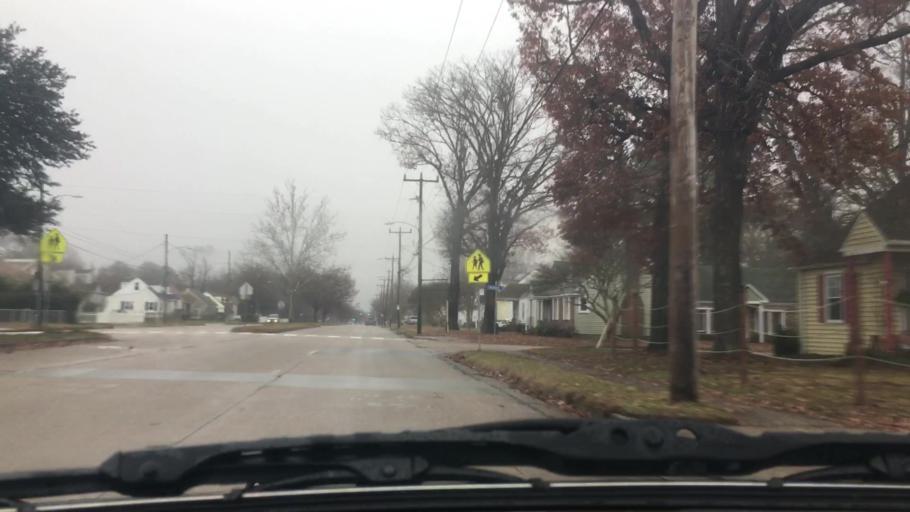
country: US
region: Virginia
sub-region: City of Norfolk
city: Norfolk
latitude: 36.9367
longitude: -76.2544
